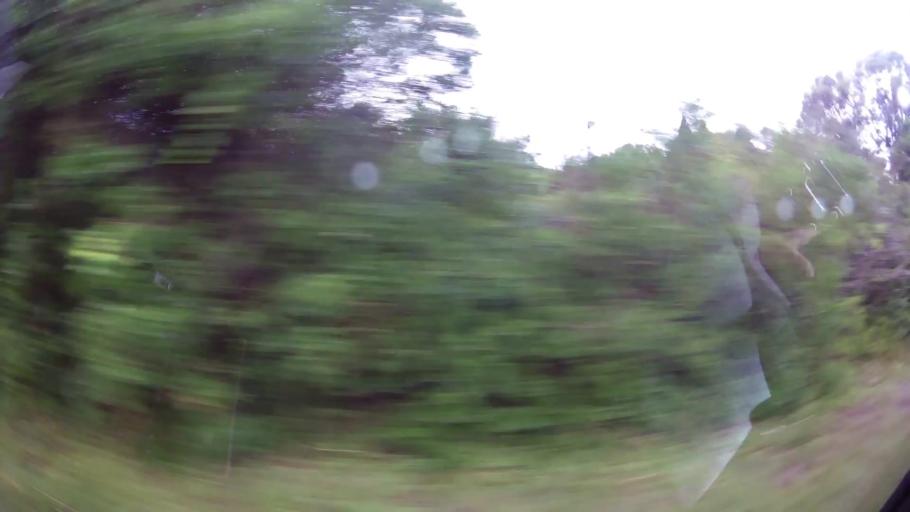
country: ZA
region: Eastern Cape
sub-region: Nelson Mandela Bay Metropolitan Municipality
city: Port Elizabeth
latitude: -34.0158
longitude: 25.5149
